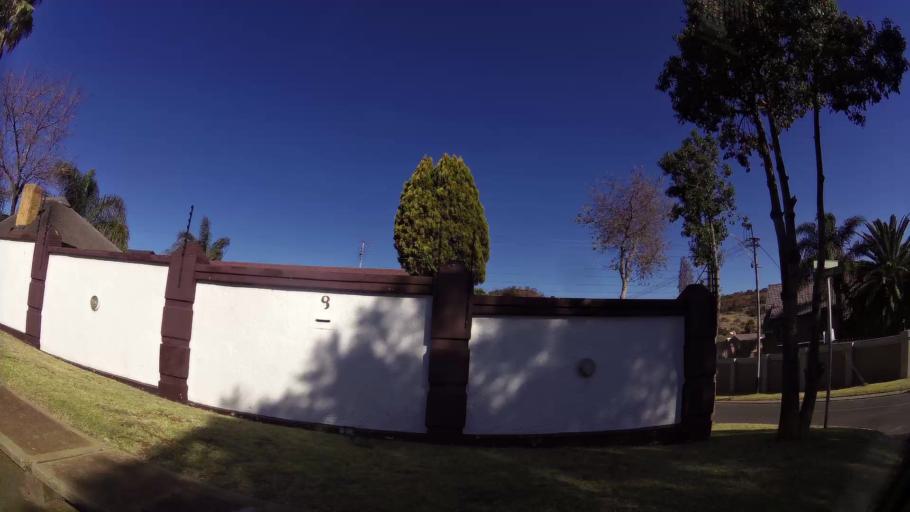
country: ZA
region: Gauteng
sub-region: City of Johannesburg Metropolitan Municipality
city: Johannesburg
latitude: -26.2763
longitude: 28.0281
